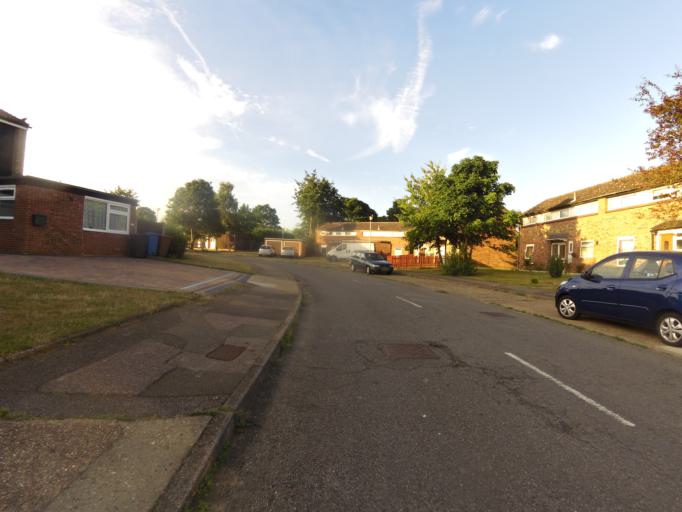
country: GB
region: England
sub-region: Suffolk
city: Ipswich
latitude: 52.0398
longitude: 1.1300
